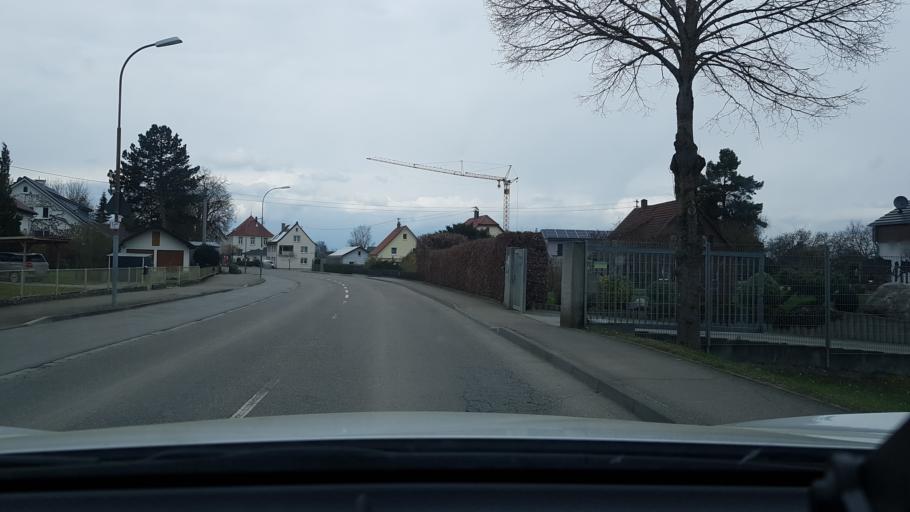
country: DE
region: Baden-Wuerttemberg
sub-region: Tuebingen Region
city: Oberstadion
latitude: 48.1854
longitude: 9.6956
